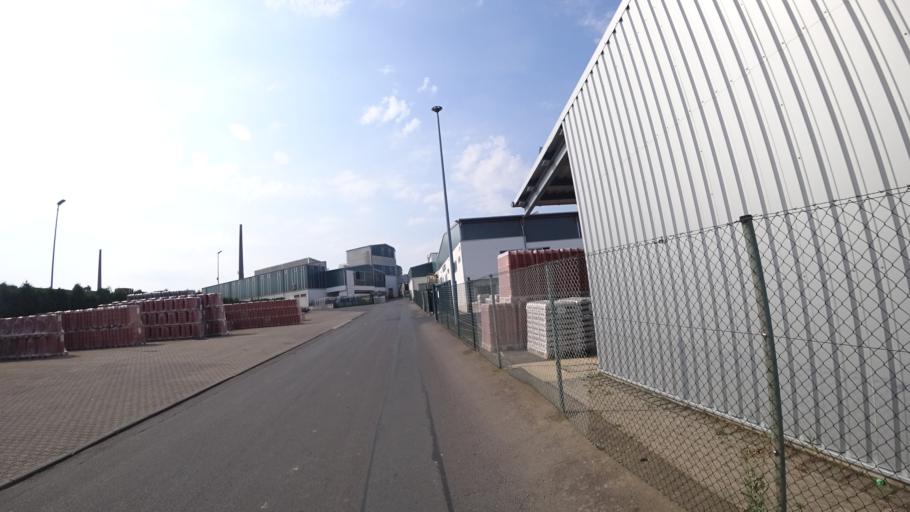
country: DE
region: Rheinland-Pfalz
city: Hundsdorf
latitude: 50.4614
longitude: 7.7206
